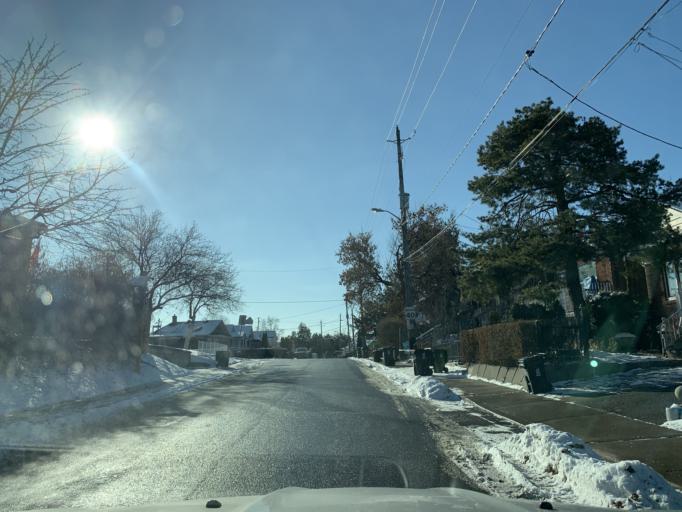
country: CA
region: Ontario
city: Toronto
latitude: 43.6804
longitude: -79.4774
